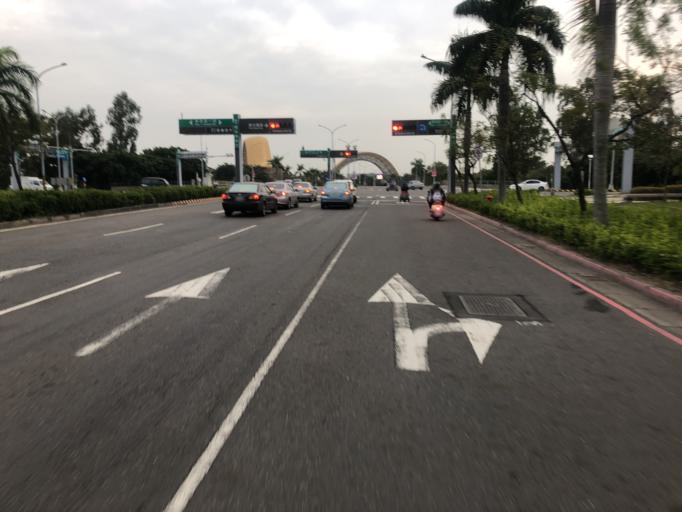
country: TW
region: Taiwan
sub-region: Tainan
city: Tainan
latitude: 23.0914
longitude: 120.2822
